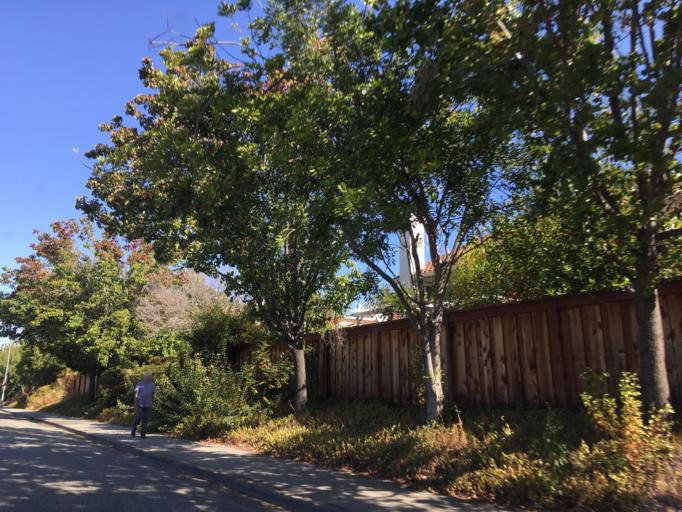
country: US
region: California
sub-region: Santa Clara County
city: Milpitas
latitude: 37.4226
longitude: -121.8690
